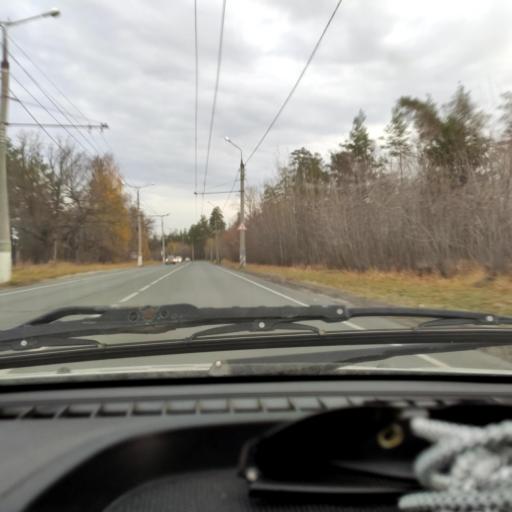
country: RU
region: Samara
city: Tol'yatti
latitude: 53.4879
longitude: 49.3832
